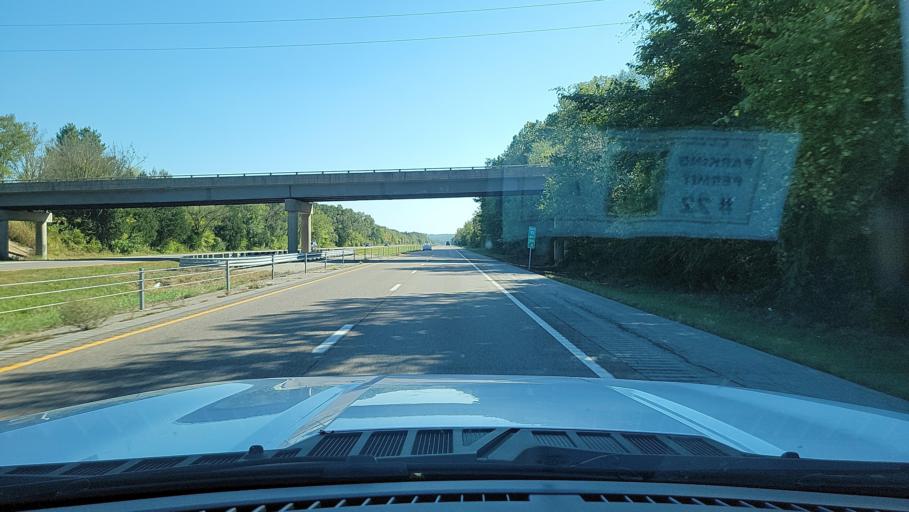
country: US
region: Missouri
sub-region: Jefferson County
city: Crystal City
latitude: 38.1102
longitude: -90.3067
